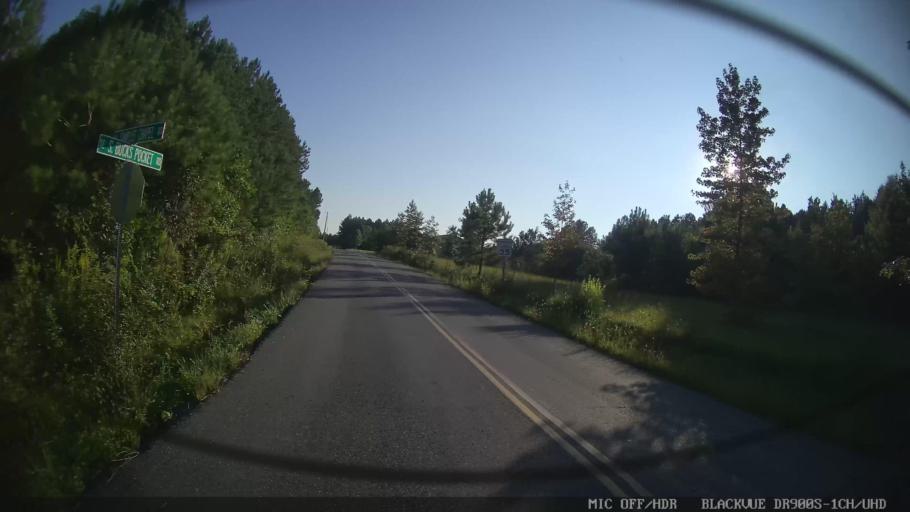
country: US
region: Tennessee
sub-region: Bradley County
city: Wildwood Lake
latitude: 35.0259
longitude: -84.7753
